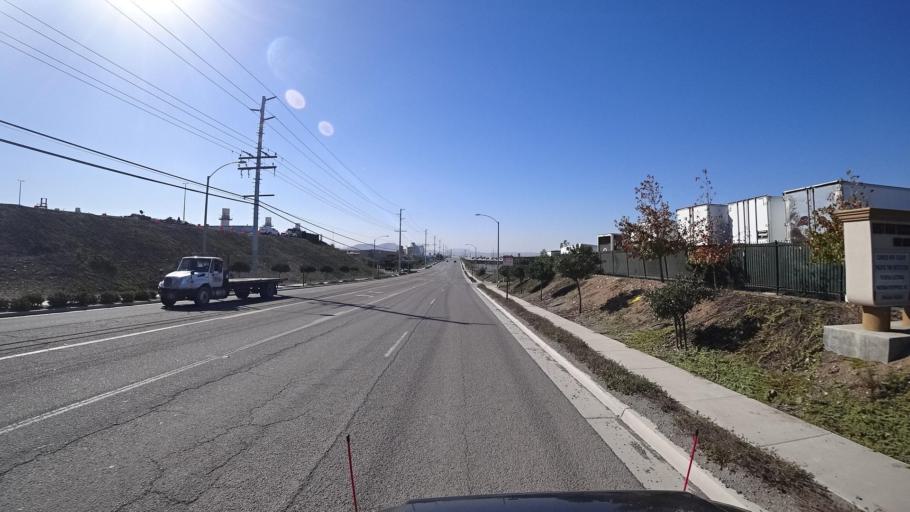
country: MX
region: Baja California
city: Tijuana
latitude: 32.5763
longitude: -116.9192
